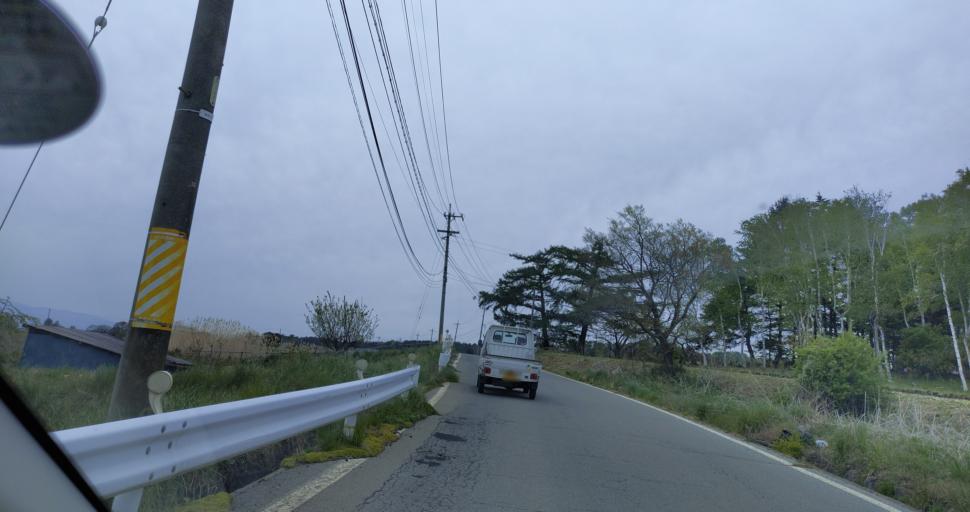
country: JP
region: Nagano
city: Komoro
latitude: 36.3366
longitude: 138.4814
